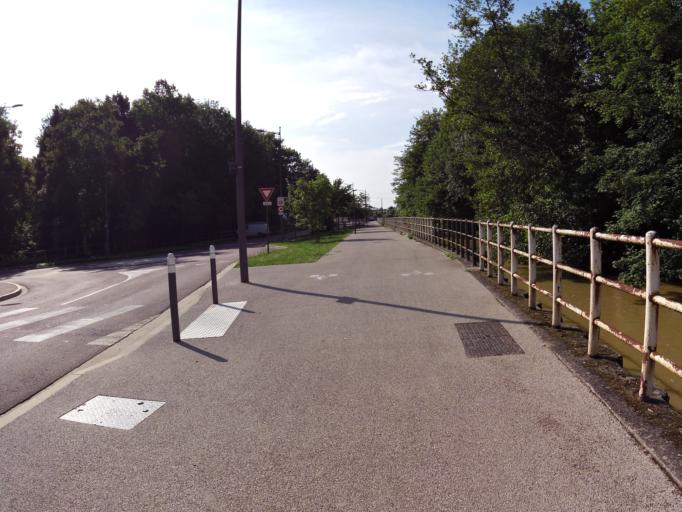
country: FR
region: Champagne-Ardenne
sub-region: Departement de l'Aube
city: Troyes
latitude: 48.2873
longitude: 4.0859
